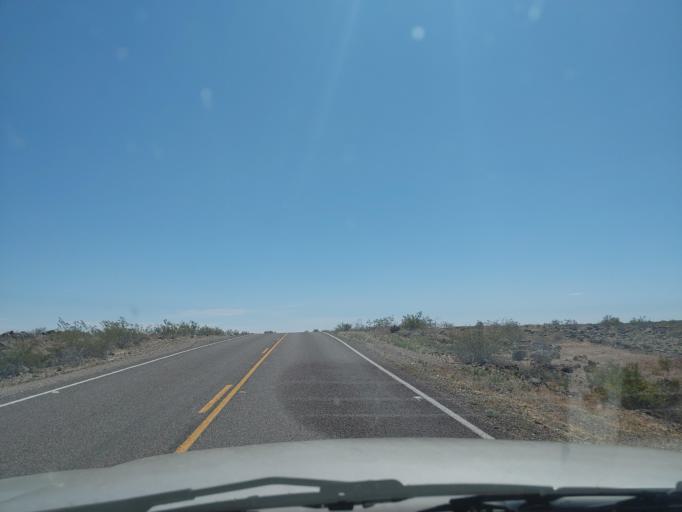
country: US
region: Arizona
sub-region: Maricopa County
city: Gila Bend
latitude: 32.9153
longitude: -113.2784
